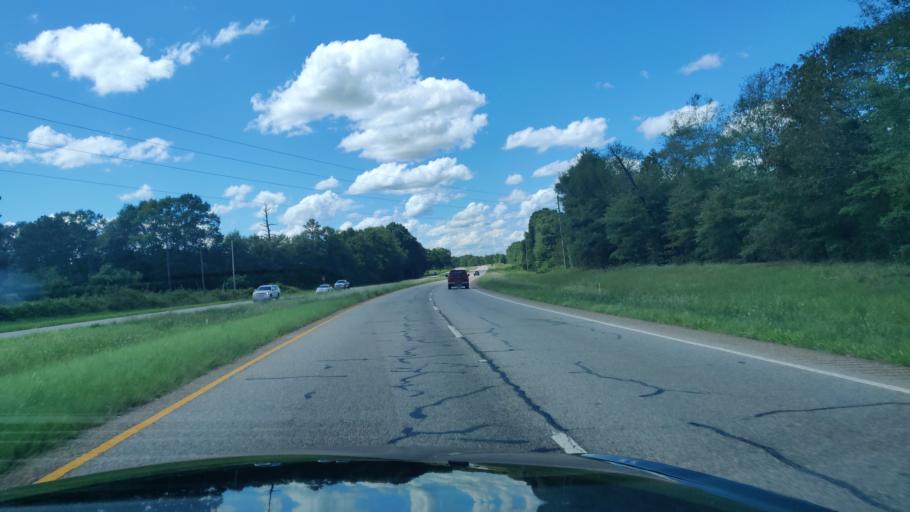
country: US
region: Georgia
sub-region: Stewart County
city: Richland
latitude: 32.0010
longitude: -84.6468
